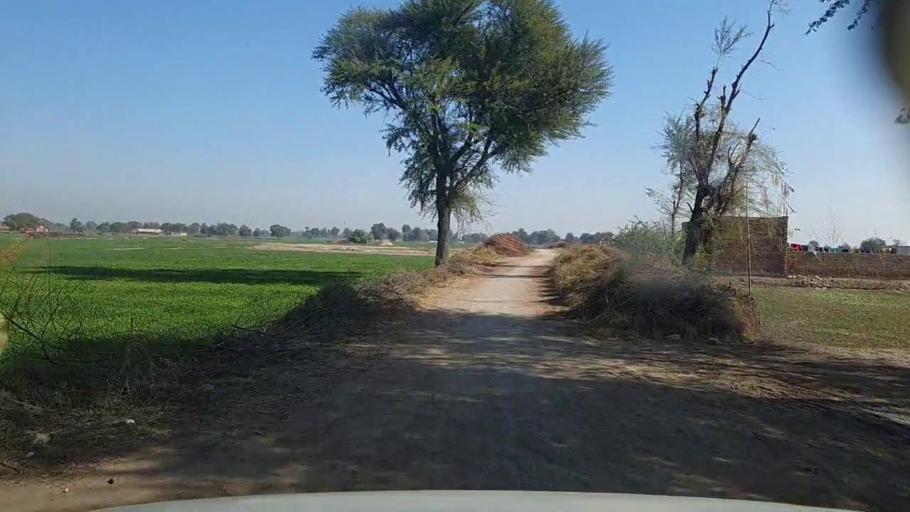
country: PK
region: Sindh
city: Khairpur
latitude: 28.0621
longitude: 69.7391
